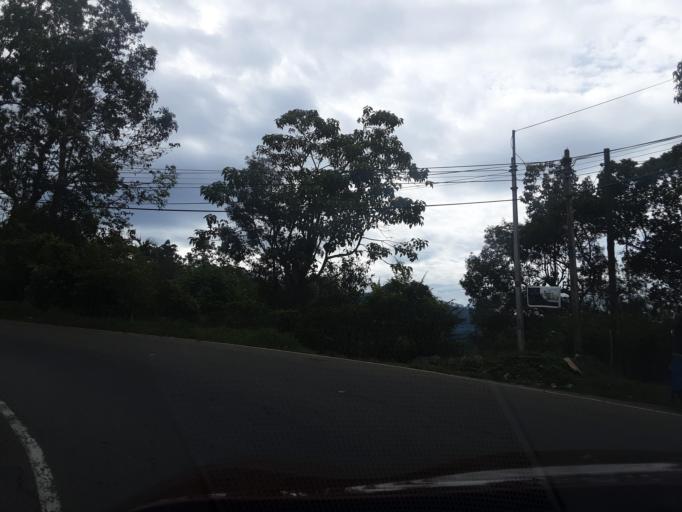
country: LK
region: Uva
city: Haputale
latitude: 6.8502
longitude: 80.9670
